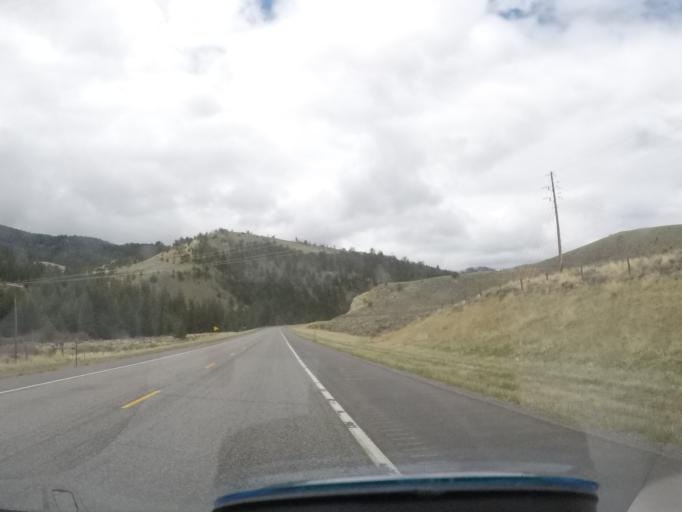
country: US
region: Wyoming
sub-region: Sublette County
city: Pinedale
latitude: 43.5791
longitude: -109.7537
